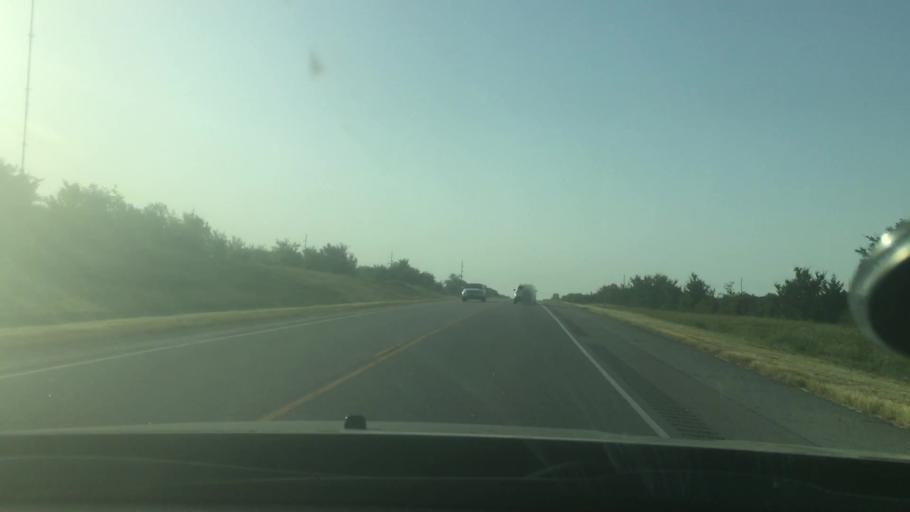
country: US
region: Oklahoma
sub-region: Pontotoc County
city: Ada
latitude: 34.6384
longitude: -96.4821
